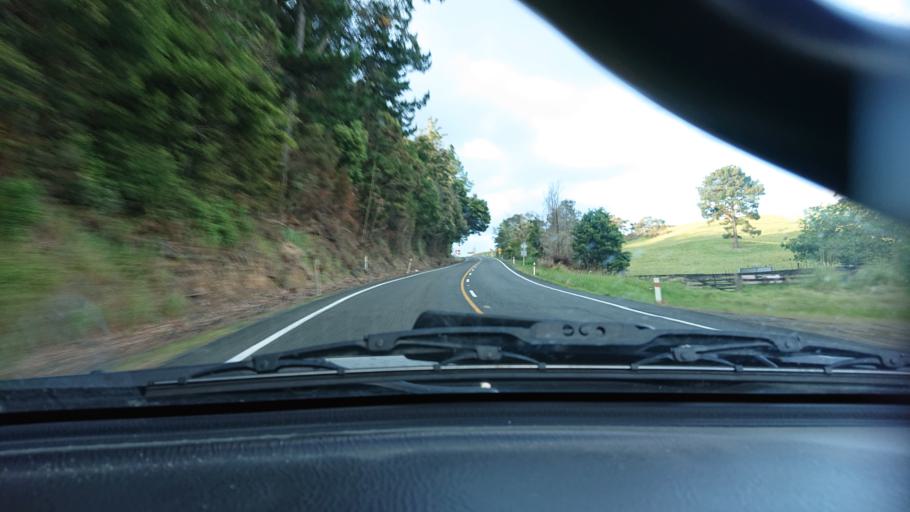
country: NZ
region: Auckland
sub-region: Auckland
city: Parakai
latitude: -36.5270
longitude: 174.4543
